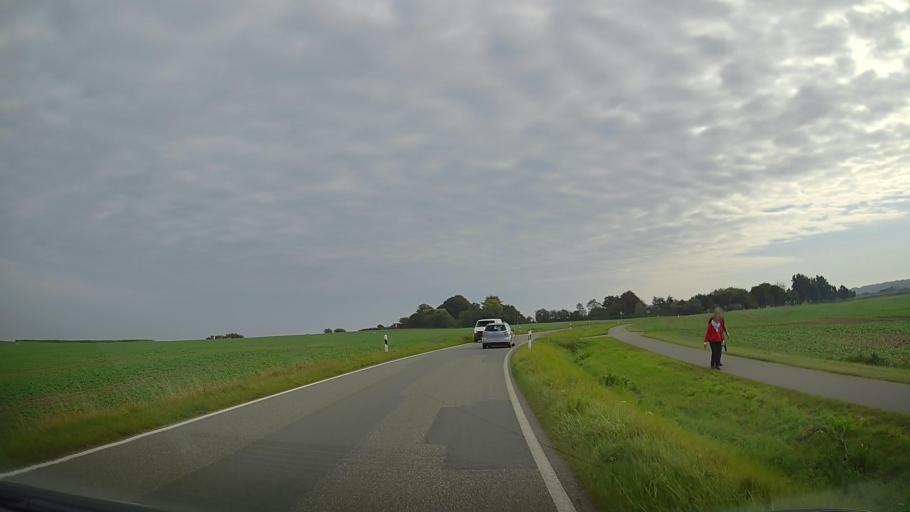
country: DE
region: Schleswig-Holstein
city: Blekendorf
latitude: 54.3401
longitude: 10.6408
